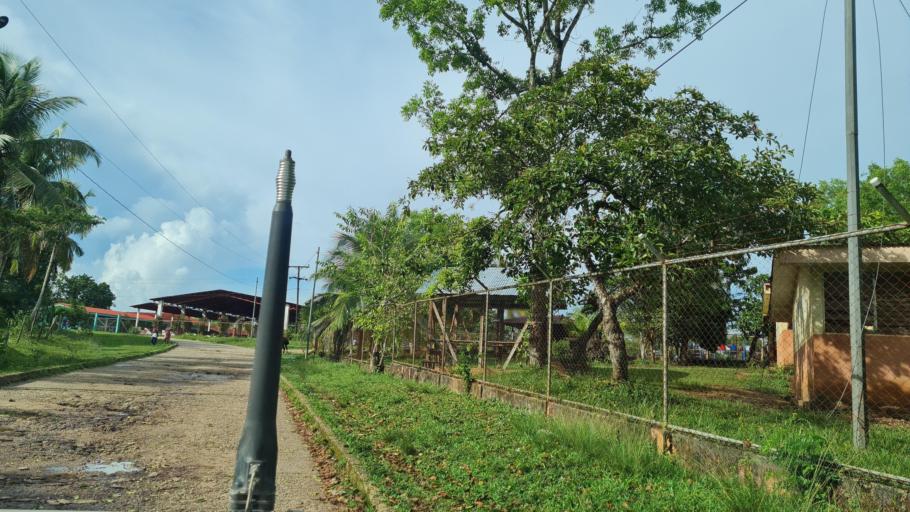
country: NI
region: Atlantico Norte (RAAN)
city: Waspam
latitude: 14.7448
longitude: -83.9691
